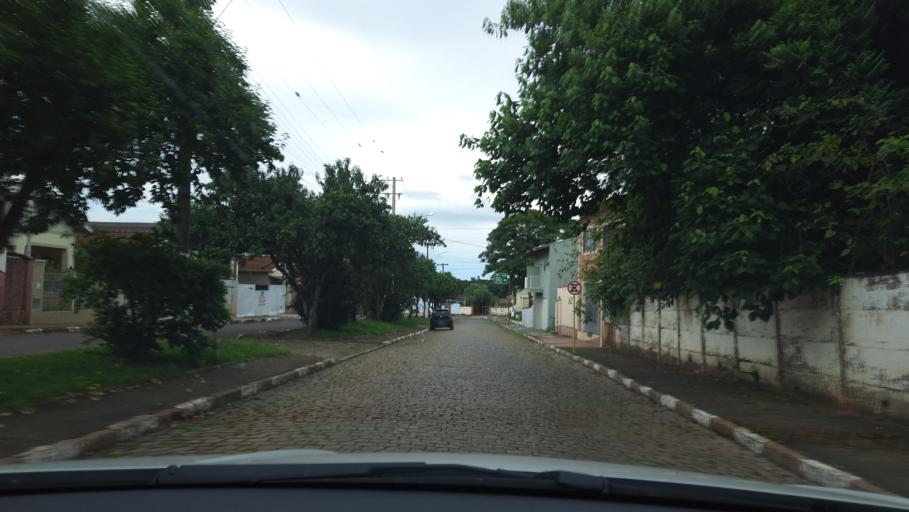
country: BR
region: Sao Paulo
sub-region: Casa Branca
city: Casa Branca
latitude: -21.7707
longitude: -47.0910
